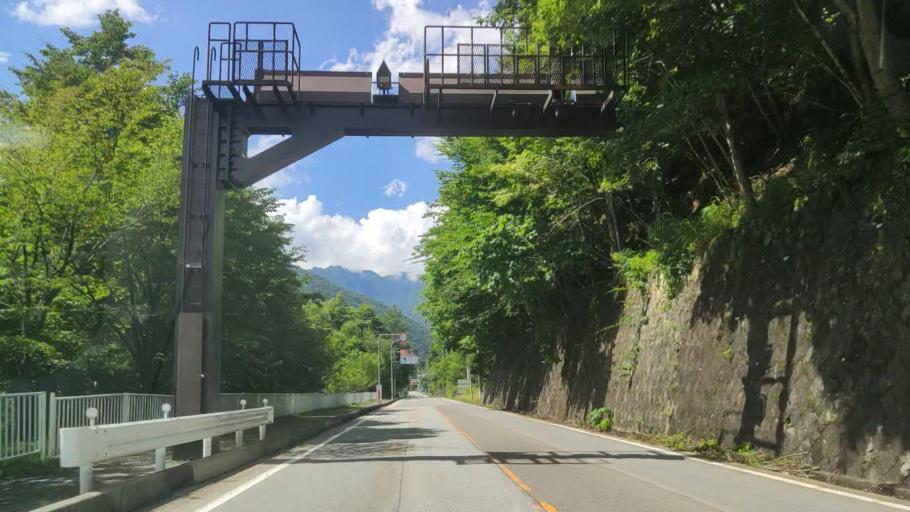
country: JP
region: Yamanashi
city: Enzan
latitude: 35.8449
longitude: 138.7633
